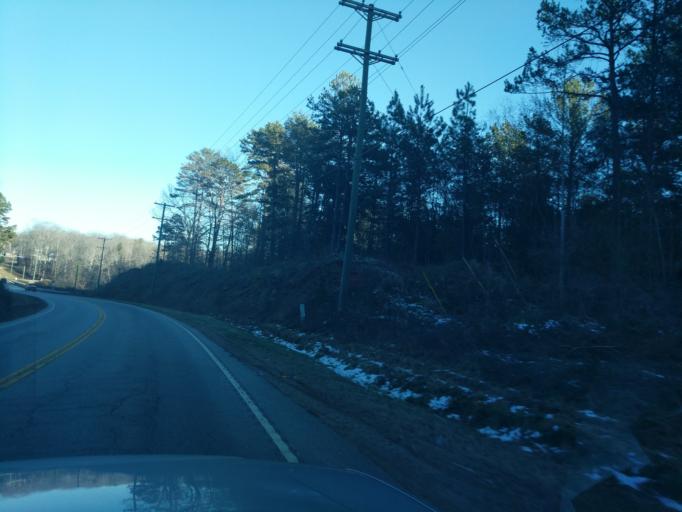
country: US
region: South Carolina
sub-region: Oconee County
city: Westminster
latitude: 34.6850
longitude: -83.1539
